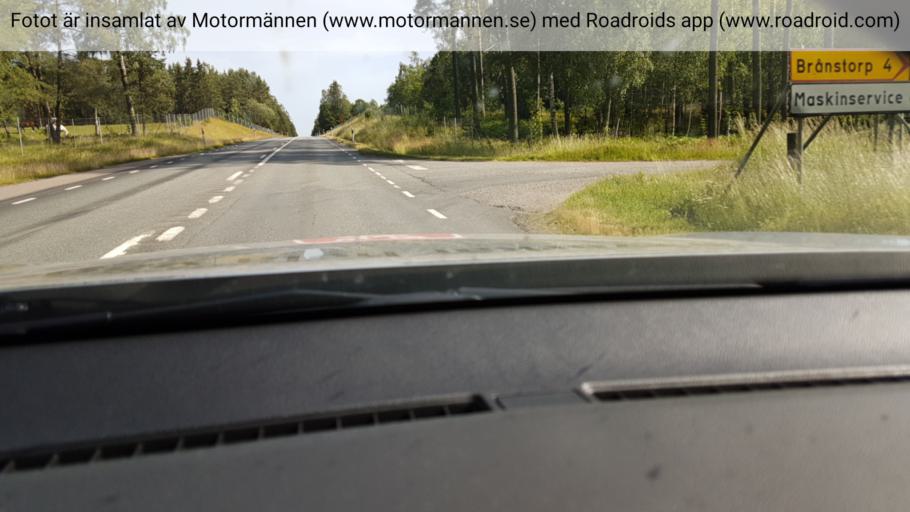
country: SE
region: Joenkoeping
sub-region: Eksjo Kommun
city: Eksjoe
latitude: 57.7213
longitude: 14.9389
